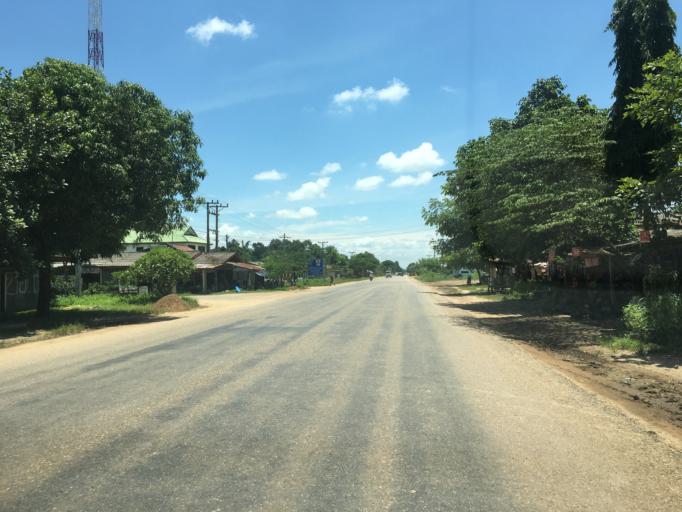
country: LA
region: Vientiane
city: Muang Phon-Hong
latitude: 18.2895
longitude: 102.4719
